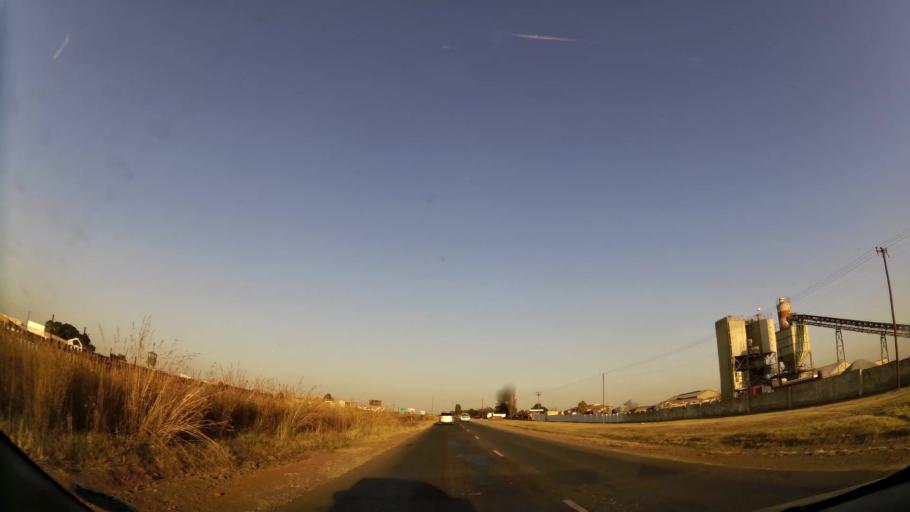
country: ZA
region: Gauteng
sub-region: West Rand District Municipality
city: Randfontein
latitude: -26.2035
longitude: 27.6870
